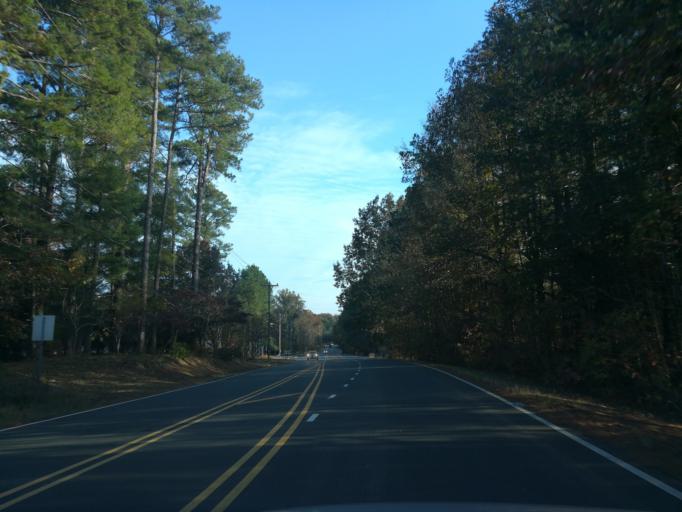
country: US
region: North Carolina
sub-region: Orange County
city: Chapel Hill
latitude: 35.9610
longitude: -78.9992
